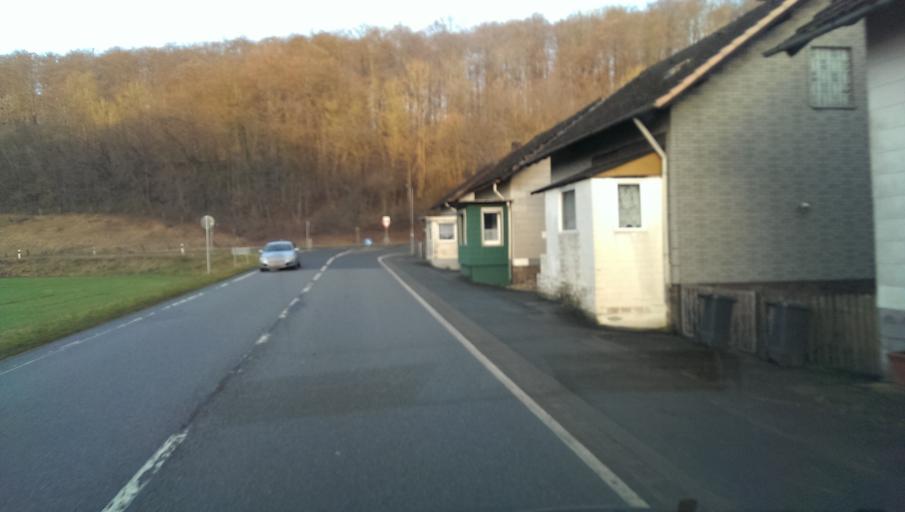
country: DE
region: Lower Saxony
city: Lenne
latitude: 51.9030
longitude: 9.6839
